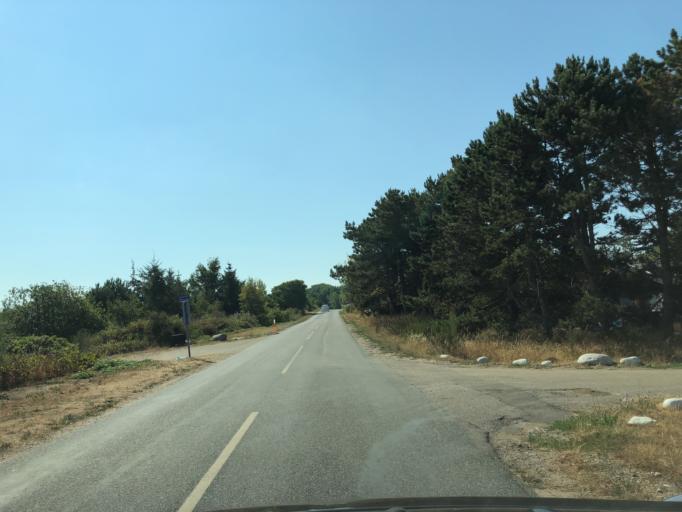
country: DK
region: Zealand
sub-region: Odsherred Kommune
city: Asnaes
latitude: 55.9905
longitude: 11.2960
